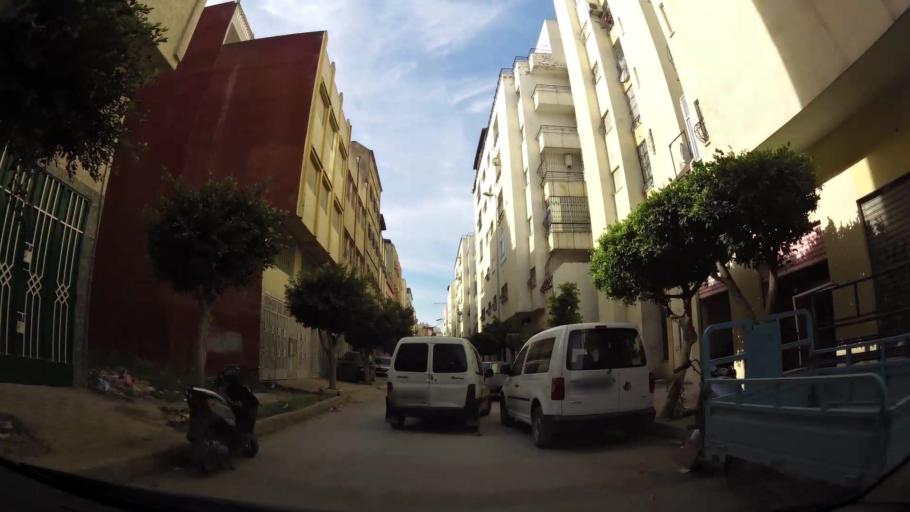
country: MA
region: Tanger-Tetouan
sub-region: Tanger-Assilah
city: Tangier
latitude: 35.7469
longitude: -5.7958
